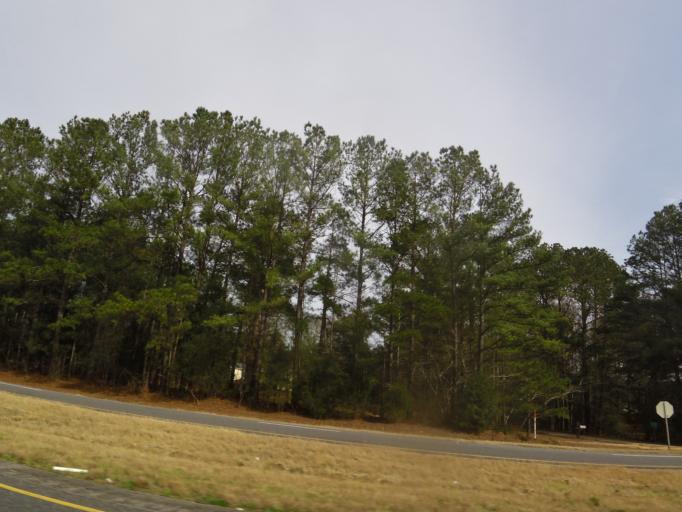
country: US
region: Alabama
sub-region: Dale County
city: Ozark
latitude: 31.5461
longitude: -85.7374
